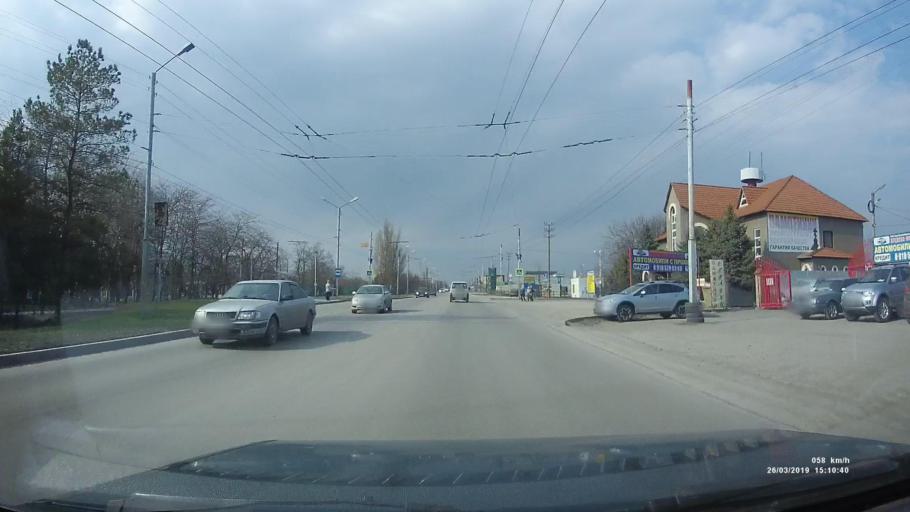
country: RU
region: Rostov
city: Taganrog
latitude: 47.2563
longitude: 38.8722
